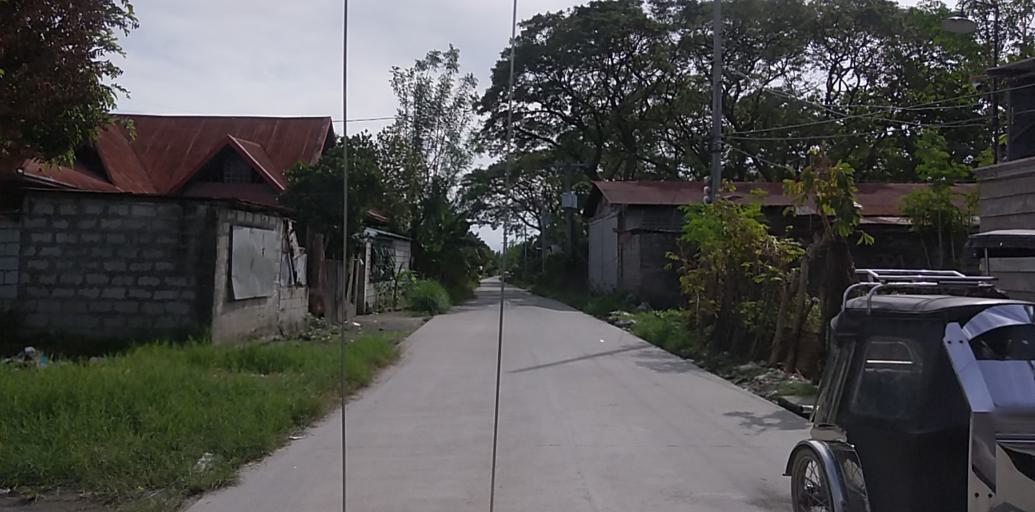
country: PH
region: Central Luzon
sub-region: Province of Pampanga
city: Angeles City
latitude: 15.1297
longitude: 120.5607
